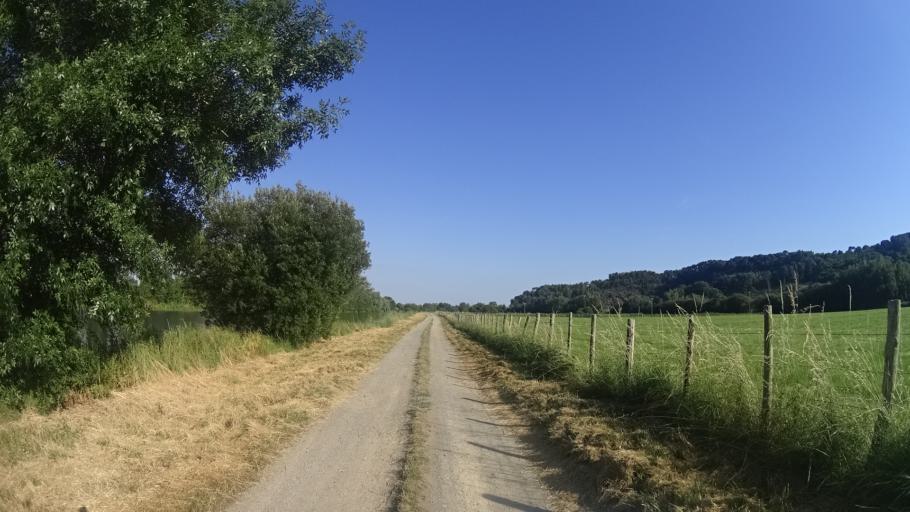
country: FR
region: Brittany
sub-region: Departement du Morbihan
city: Saint-Jean-la-Poterie
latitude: 47.6413
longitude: -2.1080
